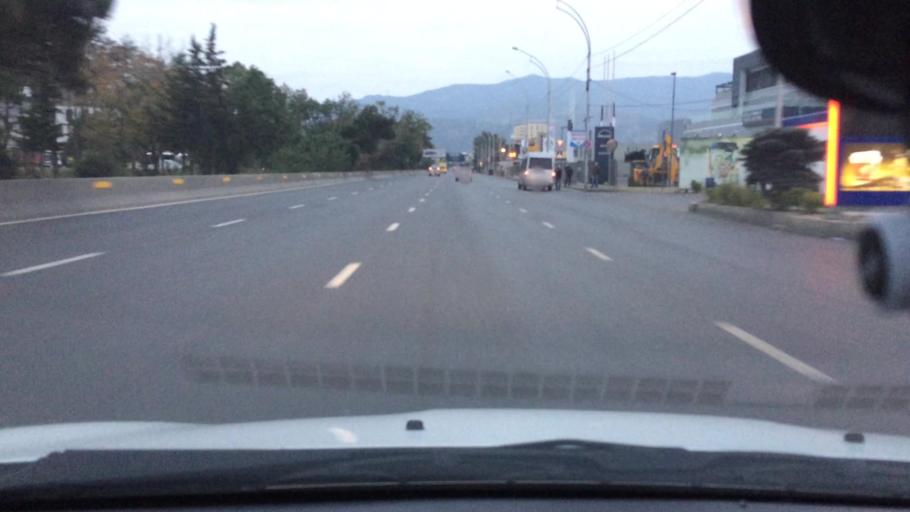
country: GE
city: Zahesi
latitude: 41.7888
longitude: 44.7702
